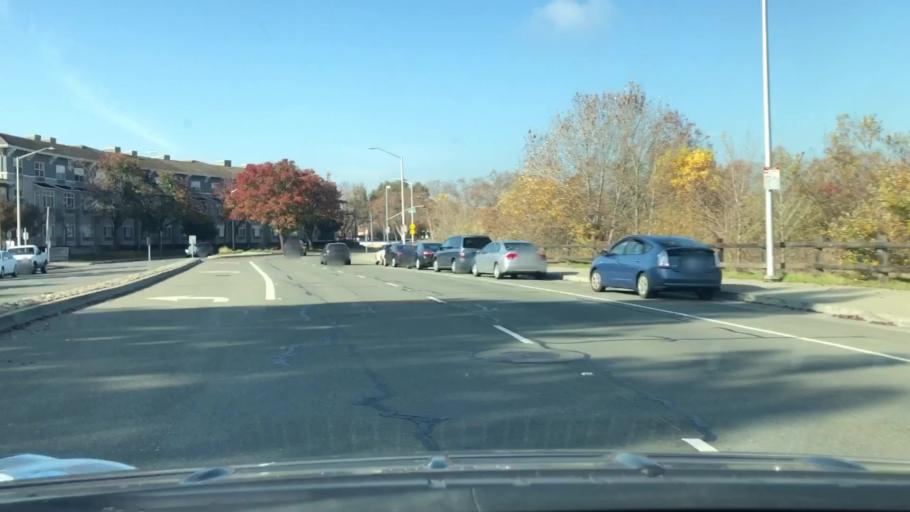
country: US
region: California
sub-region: Santa Clara County
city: Santa Clara
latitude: 37.4080
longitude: -121.9600
